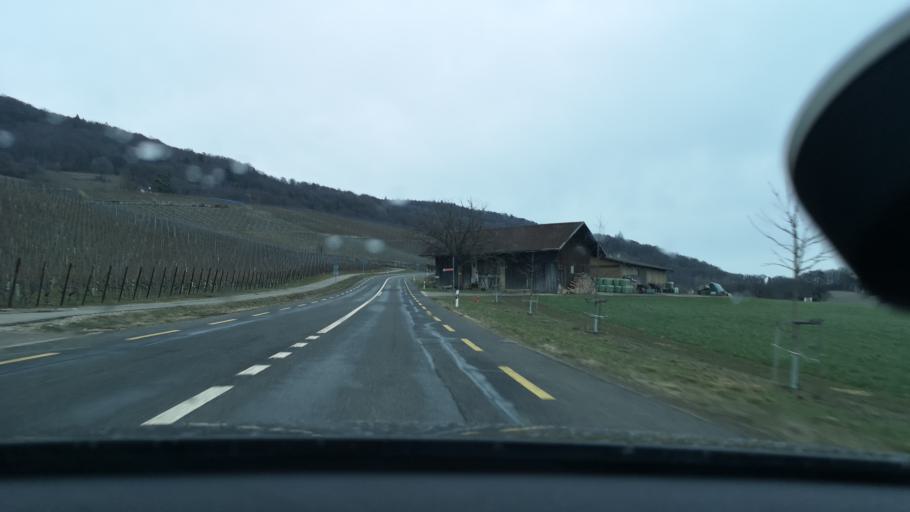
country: CH
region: Vaud
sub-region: Jura-Nord vaudois District
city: Yvonand
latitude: 46.8551
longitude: 6.7237
